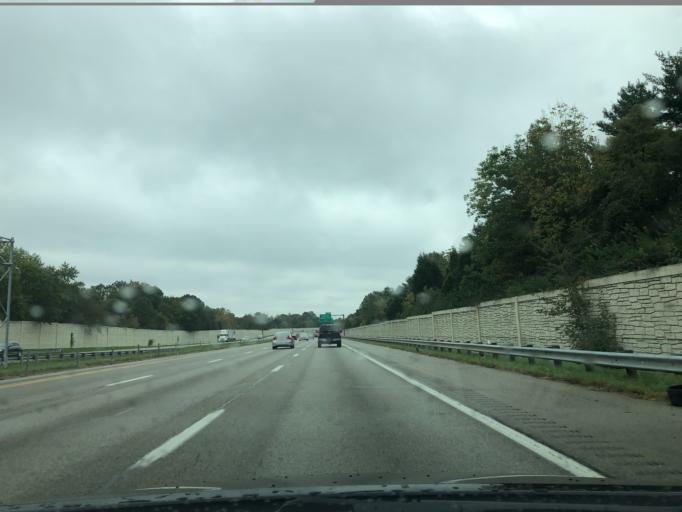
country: US
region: Ohio
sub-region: Hamilton County
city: Sixteen Mile Stand
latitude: 39.2519
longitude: -84.3201
